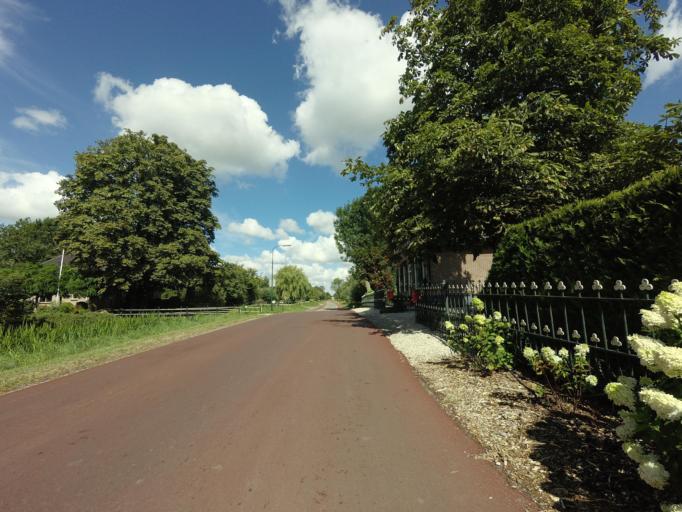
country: NL
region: Utrecht
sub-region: Stichtse Vecht
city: Breukelen
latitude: 52.1675
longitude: 4.9505
